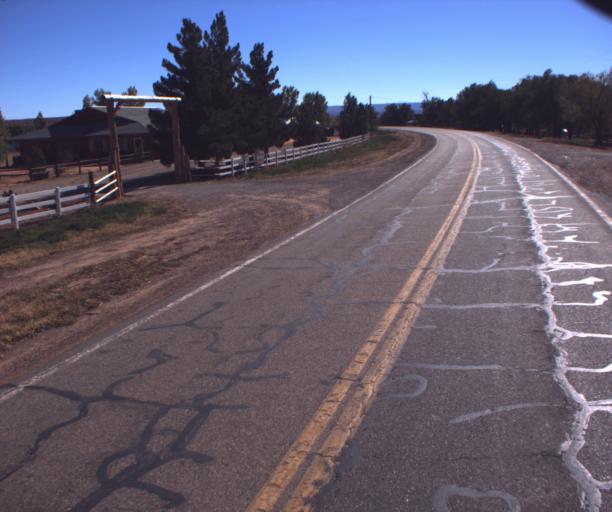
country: US
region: Arizona
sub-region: Coconino County
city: Fredonia
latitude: 36.9412
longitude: -112.5246
